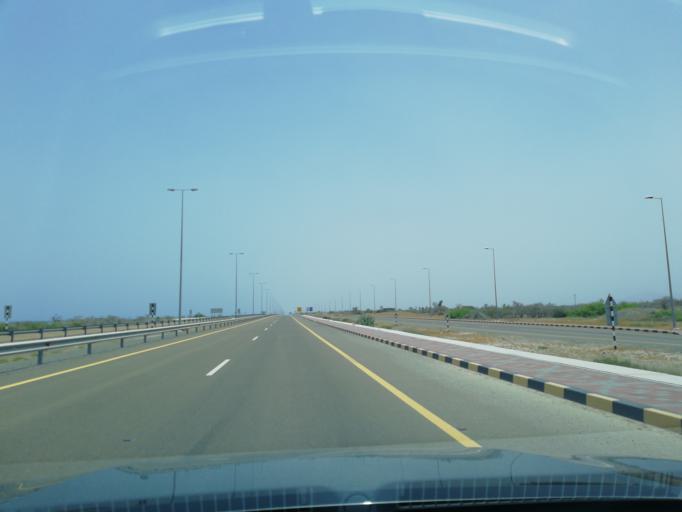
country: OM
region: Al Batinah
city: Shinas
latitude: 24.9164
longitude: 56.3891
